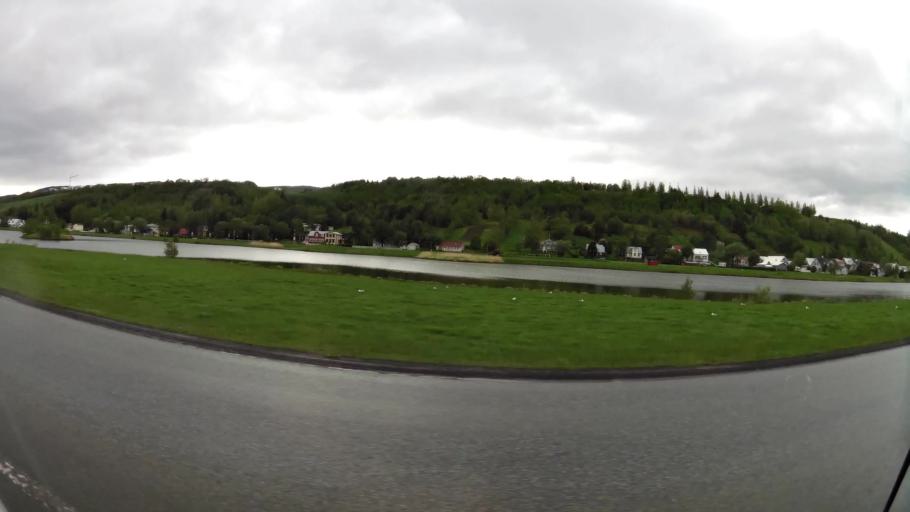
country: IS
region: Northeast
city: Akureyri
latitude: 65.6680
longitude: -18.0807
